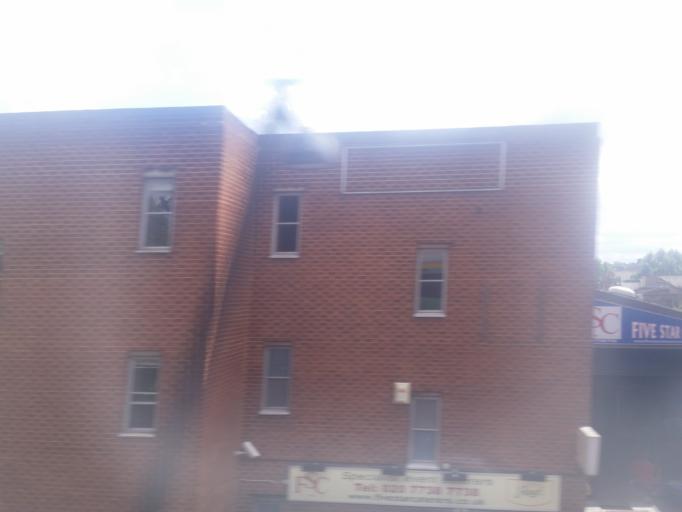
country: GB
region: England
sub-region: Greater London
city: Camberwell
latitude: 51.4728
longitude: -0.0989
